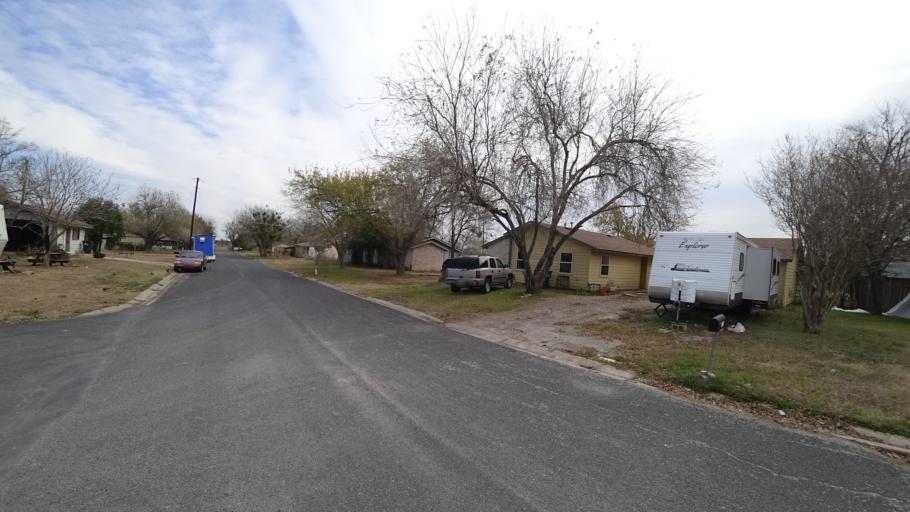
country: US
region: Texas
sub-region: Travis County
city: Onion Creek
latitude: 30.1346
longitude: -97.6777
